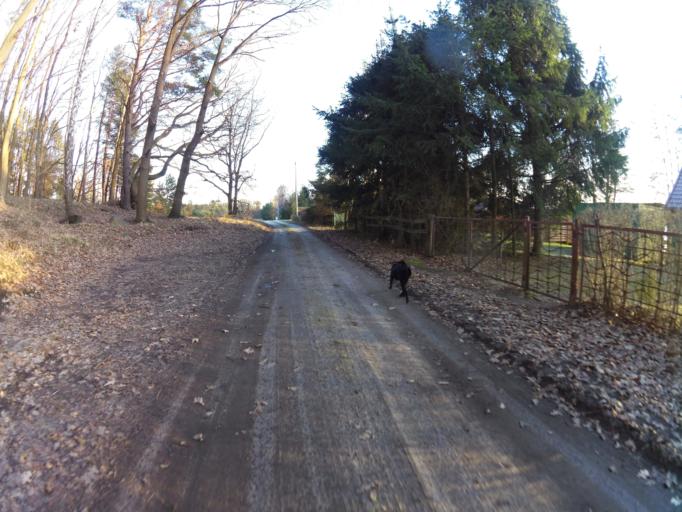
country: PL
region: West Pomeranian Voivodeship
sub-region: Powiat mysliborski
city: Debno
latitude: 52.8251
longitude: 14.7798
